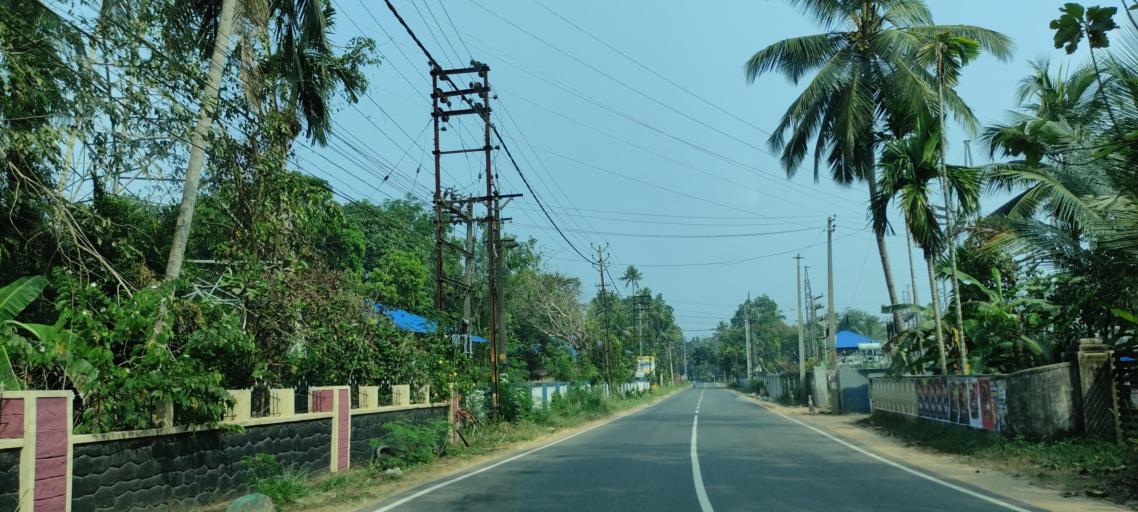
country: IN
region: Kerala
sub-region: Kottayam
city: Vaikam
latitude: 9.7617
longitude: 76.4116
